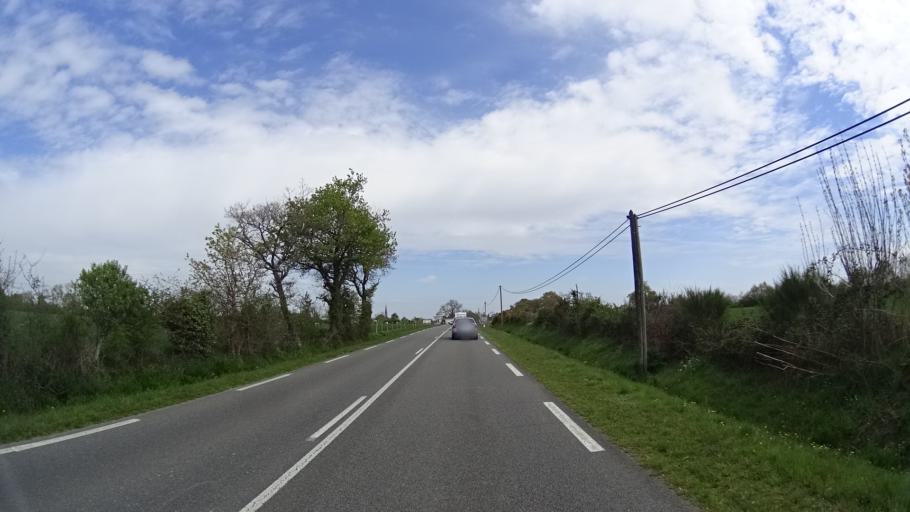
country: FR
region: Pays de la Loire
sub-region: Departement de la Loire-Atlantique
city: Sainte-Pazanne
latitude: 47.0961
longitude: -1.8235
